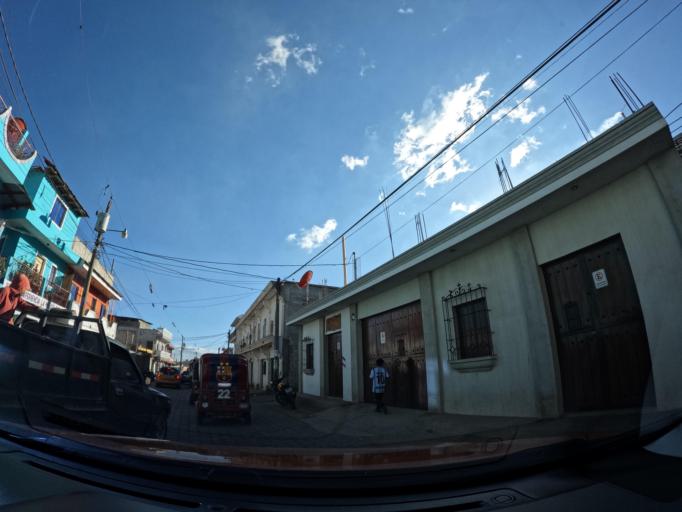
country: GT
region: Sacatepequez
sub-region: Municipio de Santa Maria de Jesus
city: Santa Maria de Jesus
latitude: 14.4911
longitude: -90.7087
